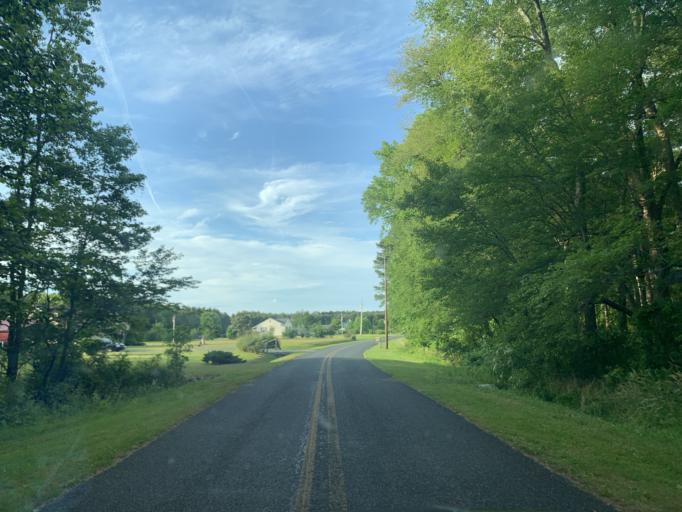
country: US
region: Maryland
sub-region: Worcester County
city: Pocomoke City
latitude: 38.0864
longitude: -75.4664
